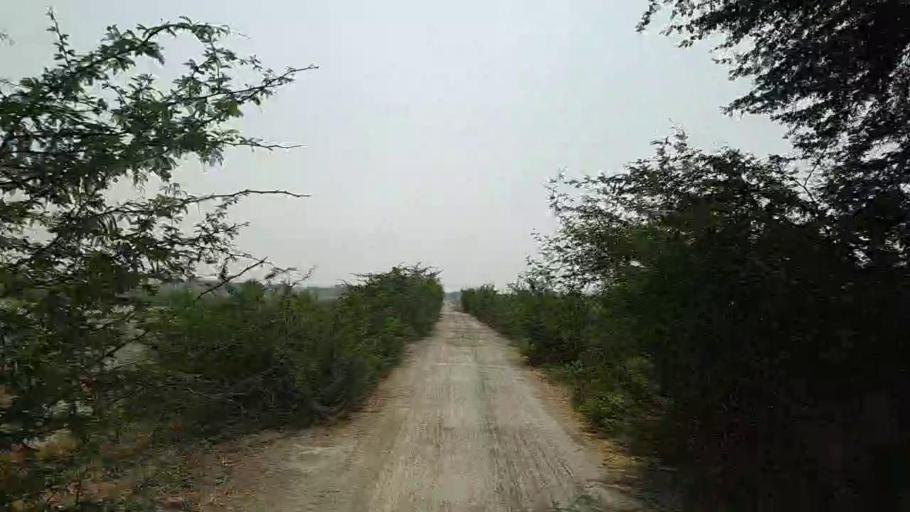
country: PK
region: Sindh
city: Naukot
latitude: 24.8119
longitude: 69.3993
